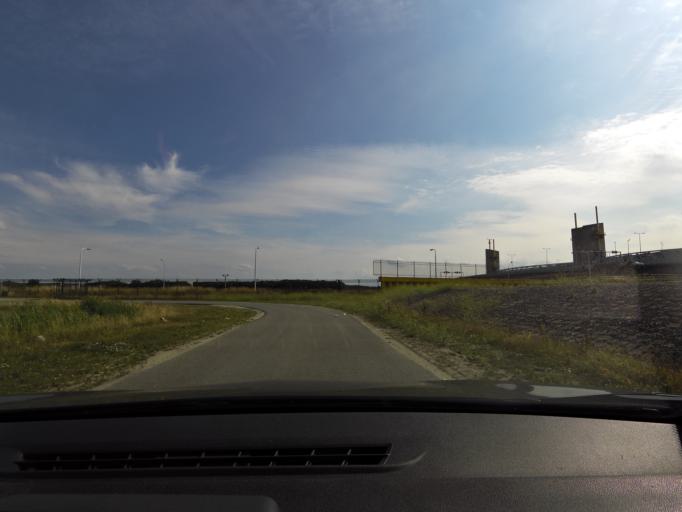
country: NL
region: South Holland
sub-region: Gemeente Spijkenisse
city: Spijkenisse
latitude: 51.8674
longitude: 4.3088
